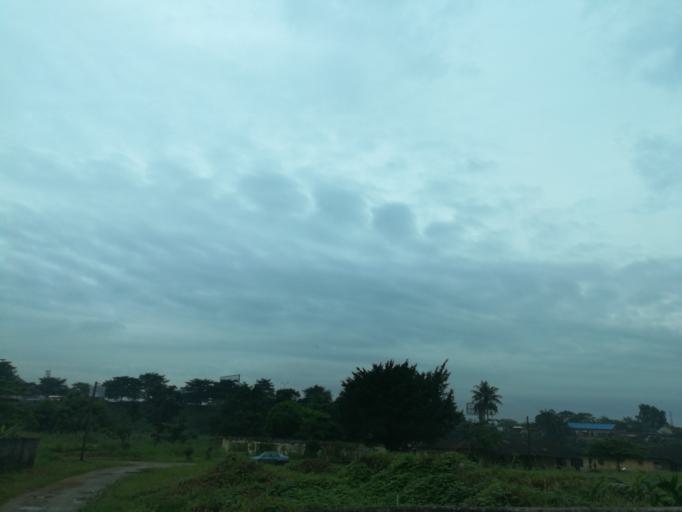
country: NG
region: Rivers
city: Port Harcourt
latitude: 4.8075
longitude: 7.0120
